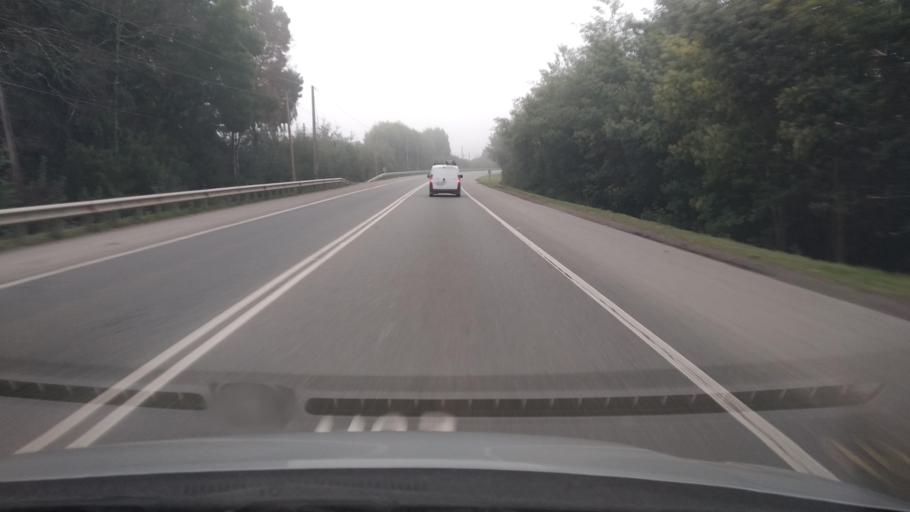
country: CL
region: Los Lagos
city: Las Animas
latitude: -39.7519
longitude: -73.2290
